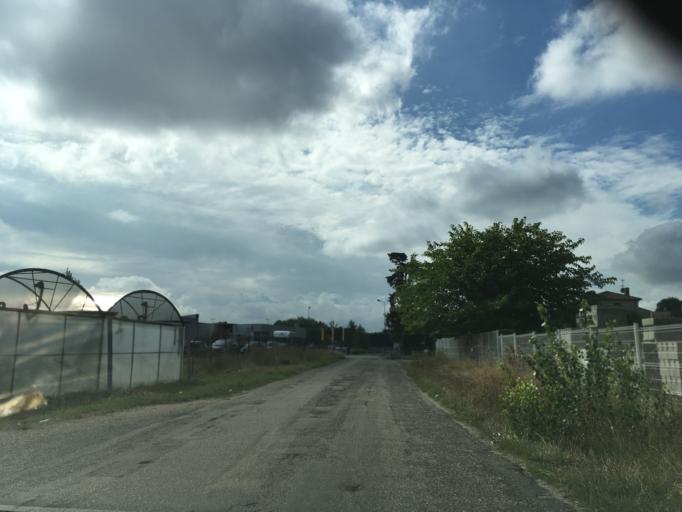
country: FR
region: Aquitaine
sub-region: Departement du Lot-et-Garonne
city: Boe
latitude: 44.1780
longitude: 0.6224
